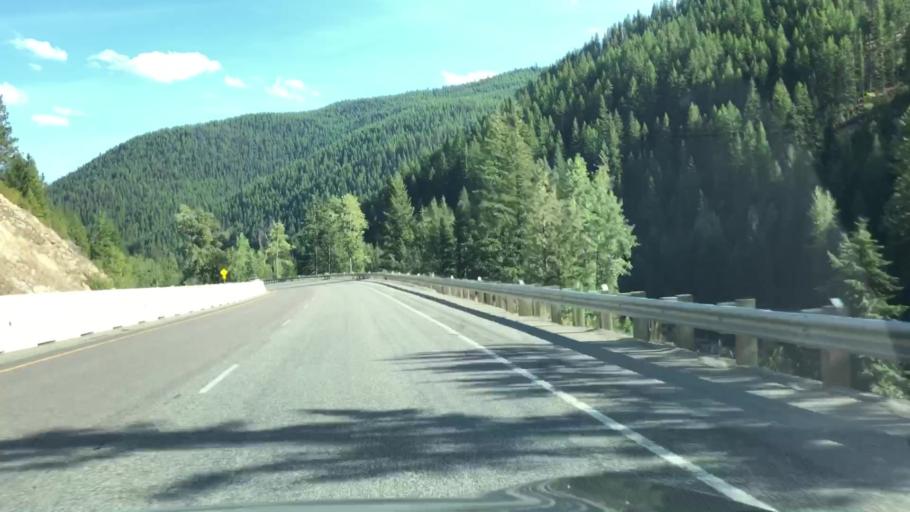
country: US
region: Montana
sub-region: Sanders County
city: Thompson Falls
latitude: 47.4000
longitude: -115.4615
